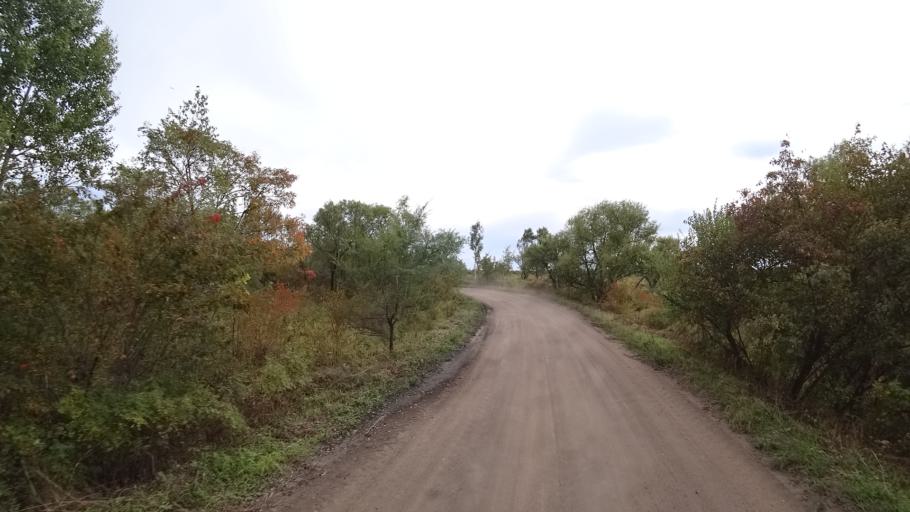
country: RU
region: Amur
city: Arkhara
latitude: 49.3476
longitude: 130.0978
